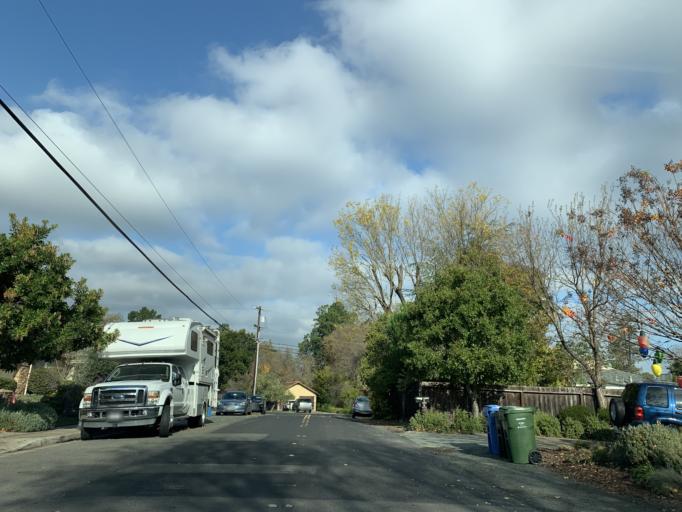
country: US
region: California
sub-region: Contra Costa County
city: Saranap
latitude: 37.8890
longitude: -122.0629
